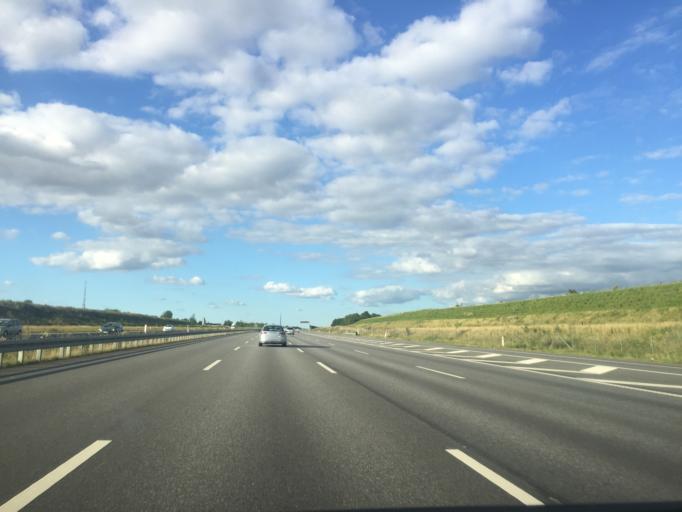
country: DK
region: Zealand
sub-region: Solrod Kommune
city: Solrod Strand
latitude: 55.5642
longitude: 12.2337
